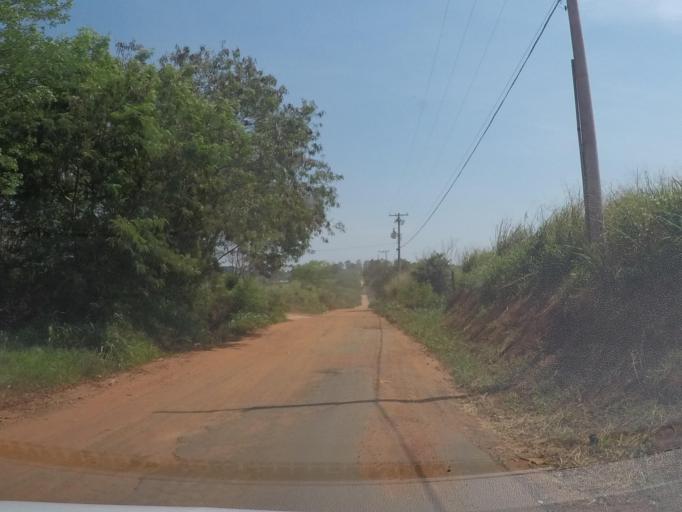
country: BR
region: Sao Paulo
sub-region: Sumare
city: Sumare
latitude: -22.8446
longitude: -47.2703
